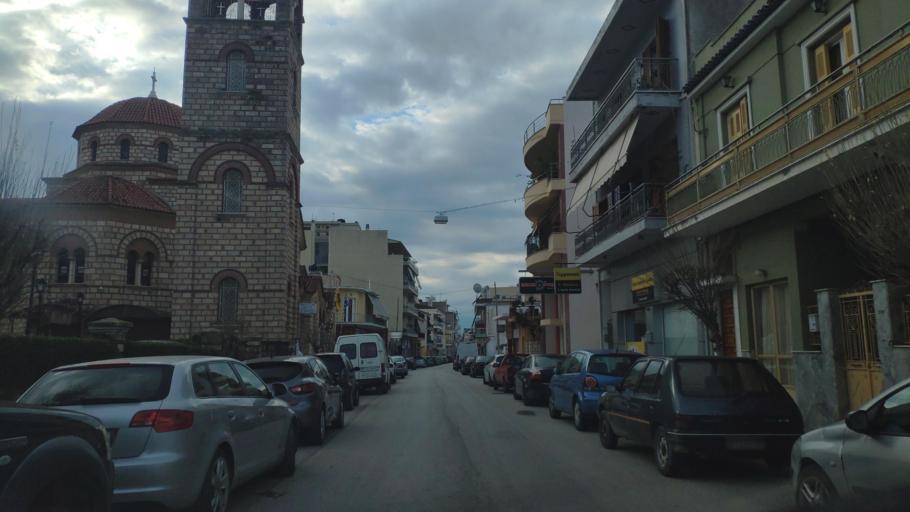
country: GR
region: Peloponnese
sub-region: Nomos Argolidos
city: Argos
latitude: 37.6417
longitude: 22.7293
